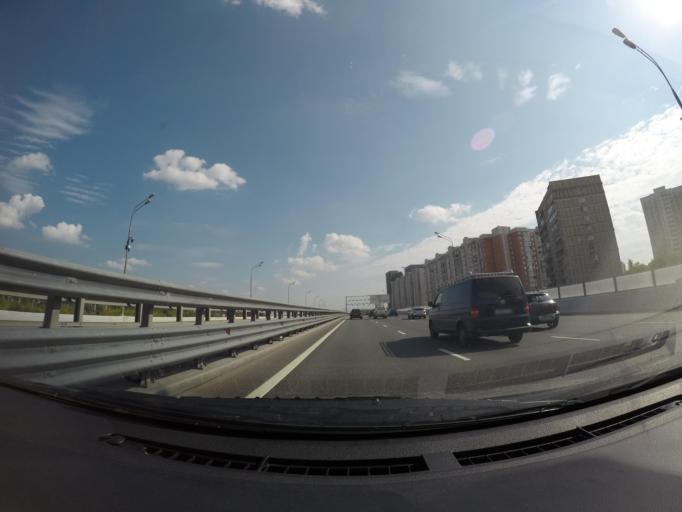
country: RU
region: Moscow
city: Novokhovrino
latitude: 55.8734
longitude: 37.4986
